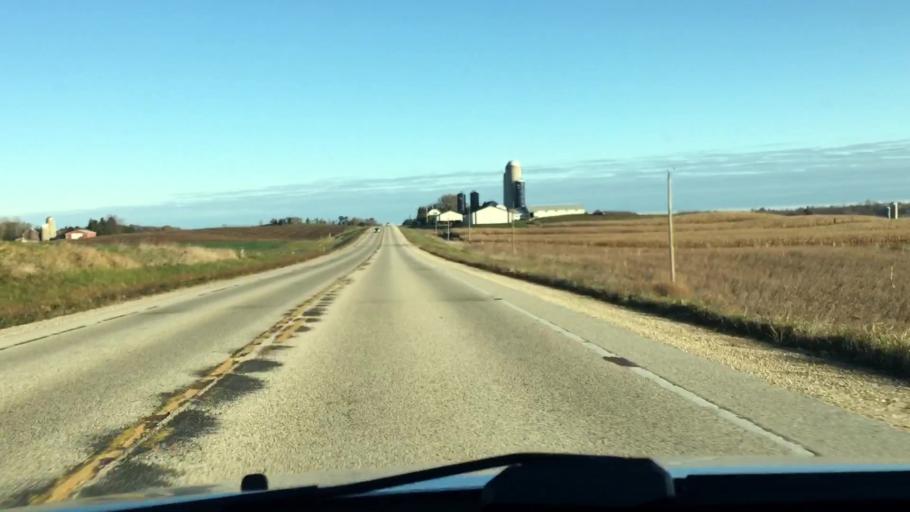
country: US
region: Wisconsin
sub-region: Dodge County
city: Theresa
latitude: 43.4495
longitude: -88.4504
